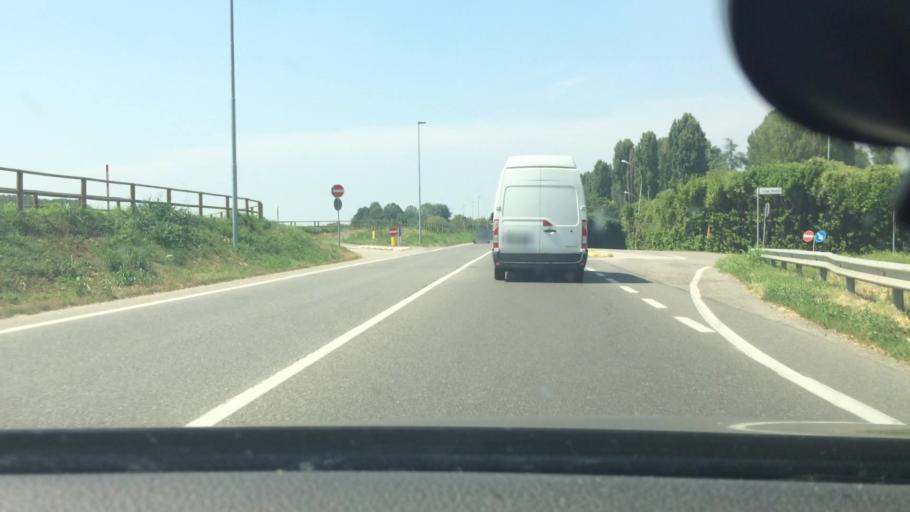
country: IT
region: Lombardy
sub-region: Provincia di Lodi
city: San Rocco al Porto
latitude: 45.0744
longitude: 9.7064
